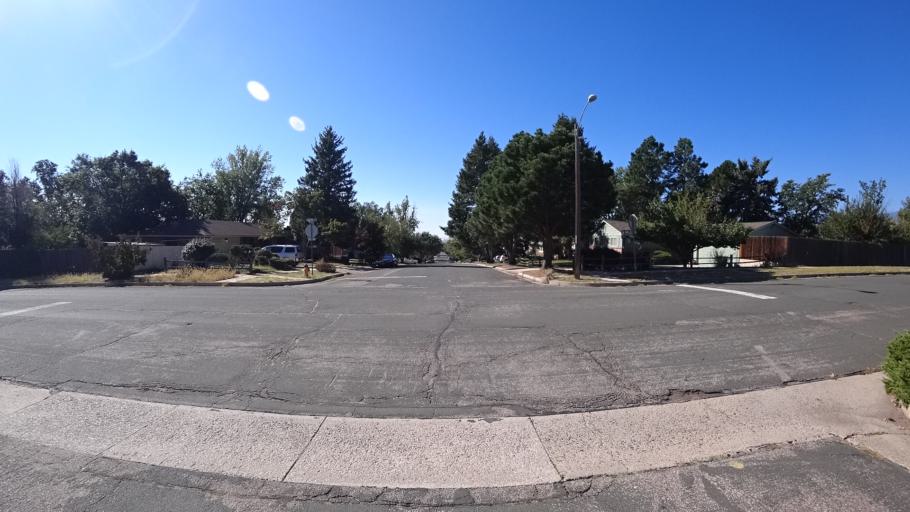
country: US
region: Colorado
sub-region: El Paso County
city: Cimarron Hills
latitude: 38.8655
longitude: -104.7619
